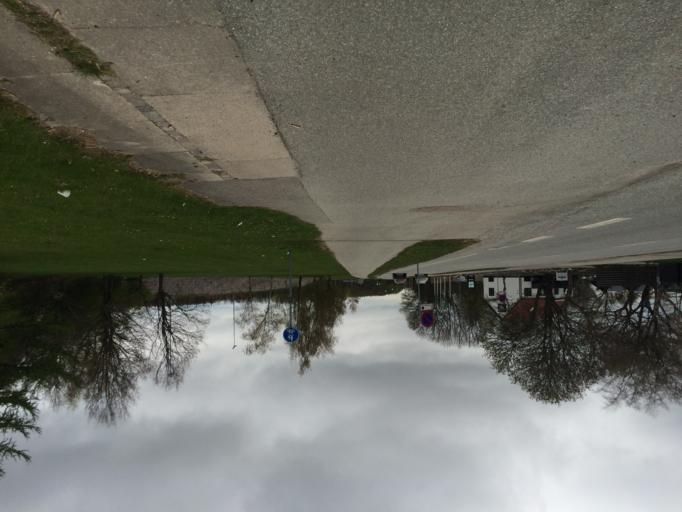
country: DK
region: Capital Region
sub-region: Vallensbaek Kommune
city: Vallensbaek
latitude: 55.6276
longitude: 12.3712
